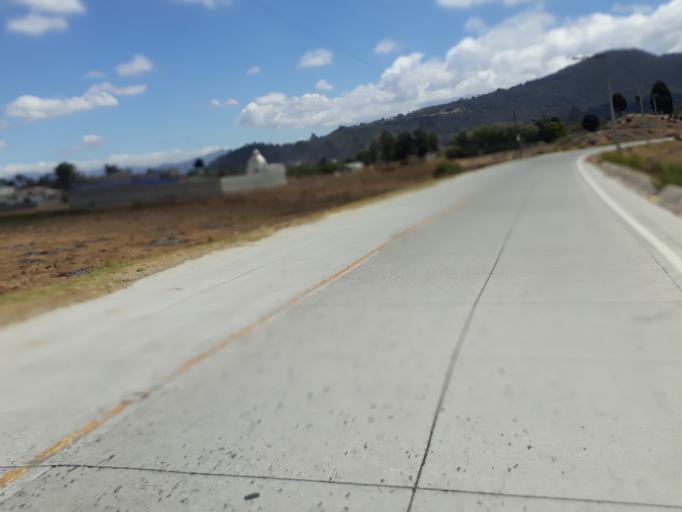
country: GT
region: Quetzaltenango
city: Quetzaltenango
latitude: 14.8156
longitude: -91.5529
